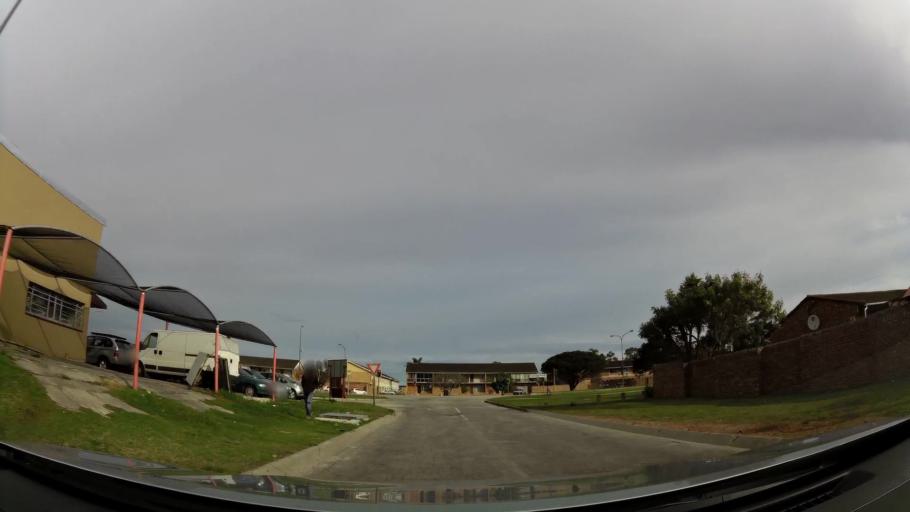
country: ZA
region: Eastern Cape
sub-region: Nelson Mandela Bay Metropolitan Municipality
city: Port Elizabeth
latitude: -33.9410
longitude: 25.5040
